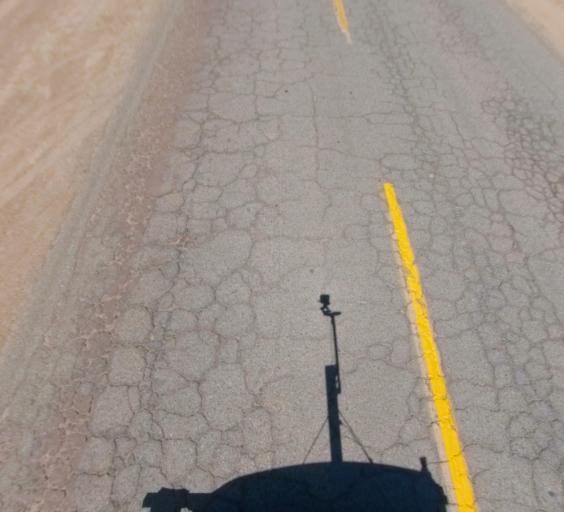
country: US
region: California
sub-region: Madera County
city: Bonadelle Ranchos-Madera Ranchos
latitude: 36.8947
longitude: -119.8265
